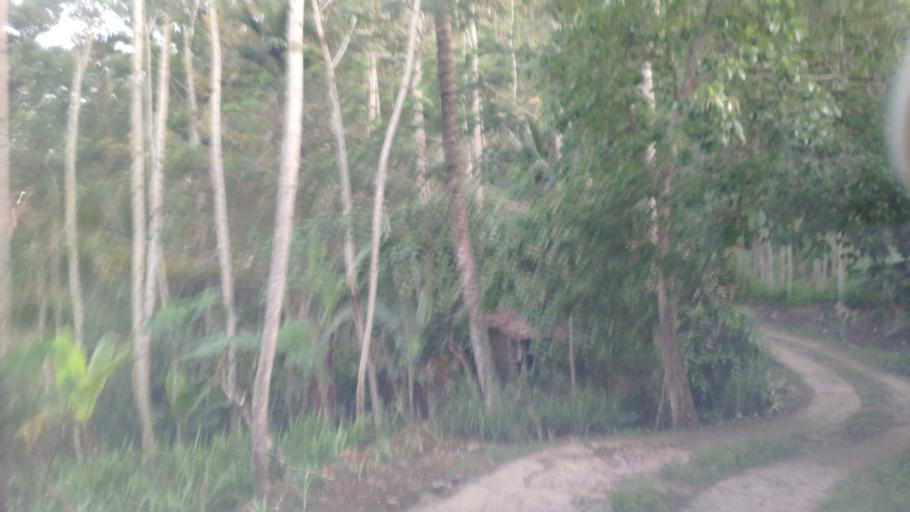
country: ID
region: Central Java
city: Buaran
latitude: -7.2598
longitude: 109.5703
